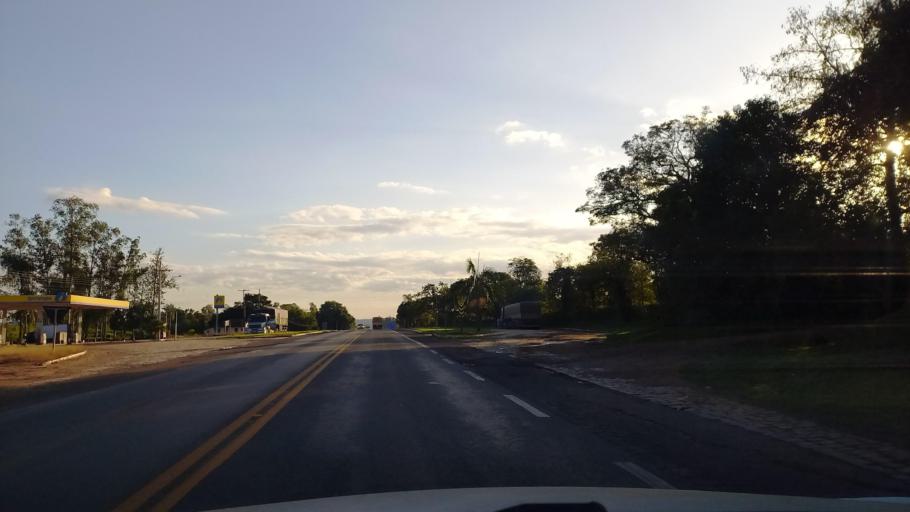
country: BR
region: Rio Grande do Sul
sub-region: Venancio Aires
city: Venancio Aires
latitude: -29.6659
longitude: -52.2674
